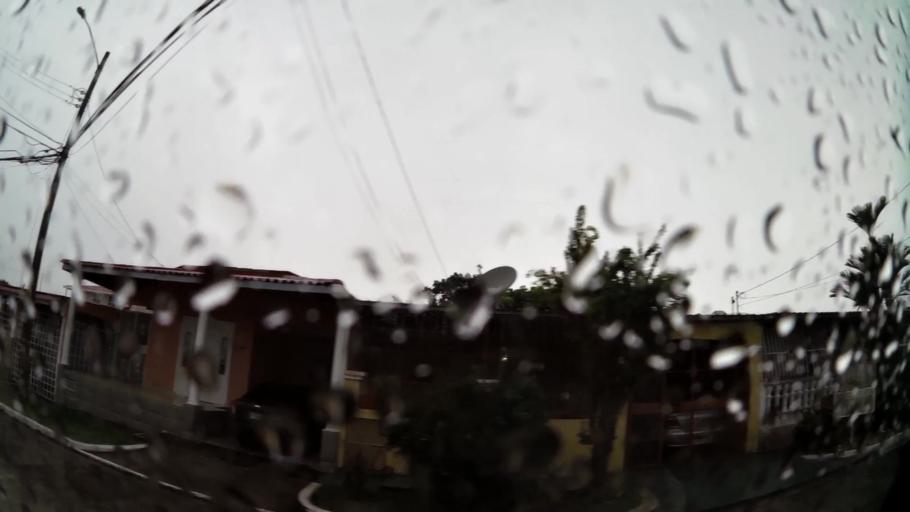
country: PA
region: Panama
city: San Miguelito
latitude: 9.0542
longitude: -79.4740
